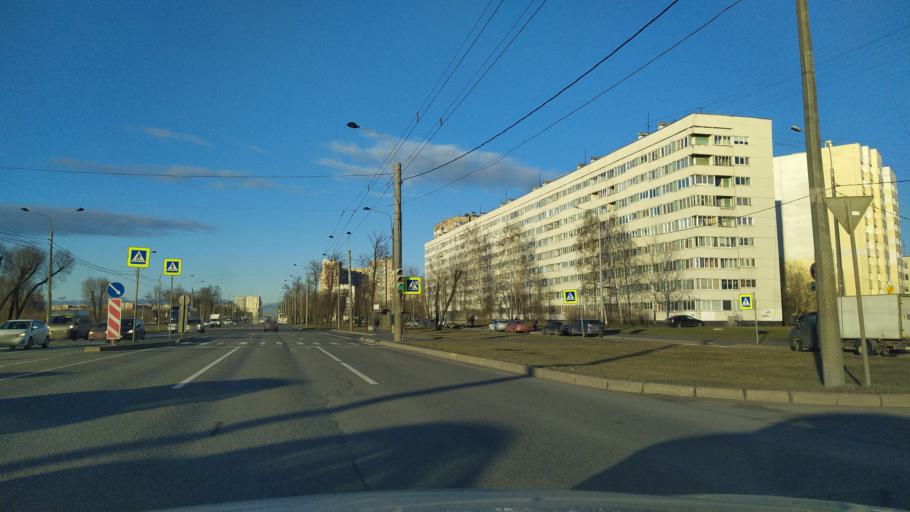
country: RU
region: St.-Petersburg
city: Uritsk
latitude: 59.8362
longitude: 30.1990
